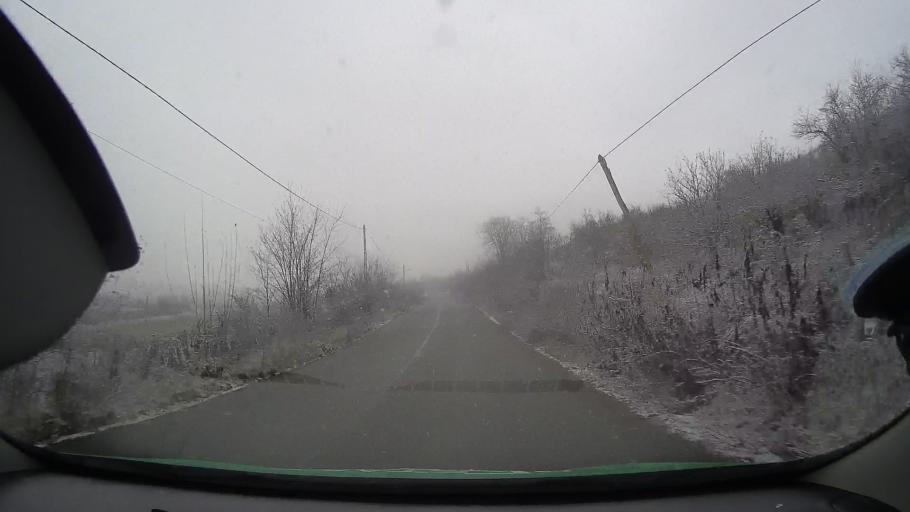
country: RO
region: Alba
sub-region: Comuna Noslac
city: Noslac
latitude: 46.3524
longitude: 23.9332
